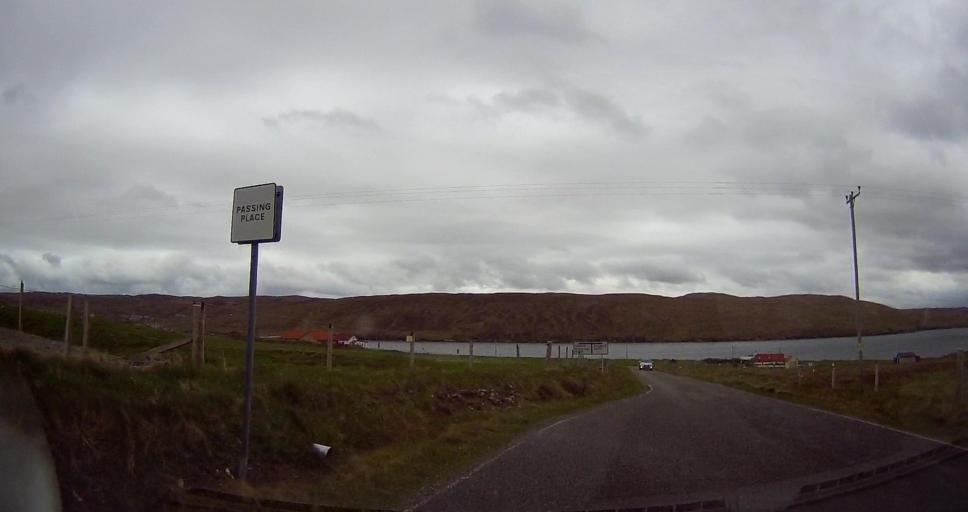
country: GB
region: Scotland
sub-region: Shetland Islands
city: Lerwick
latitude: 60.4842
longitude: -1.4769
